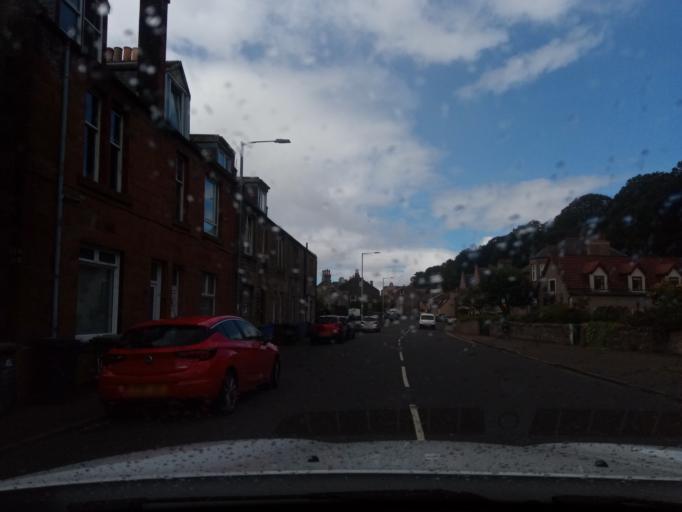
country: GB
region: Scotland
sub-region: Fife
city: High Valleyfield
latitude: 56.0595
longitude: -3.5799
